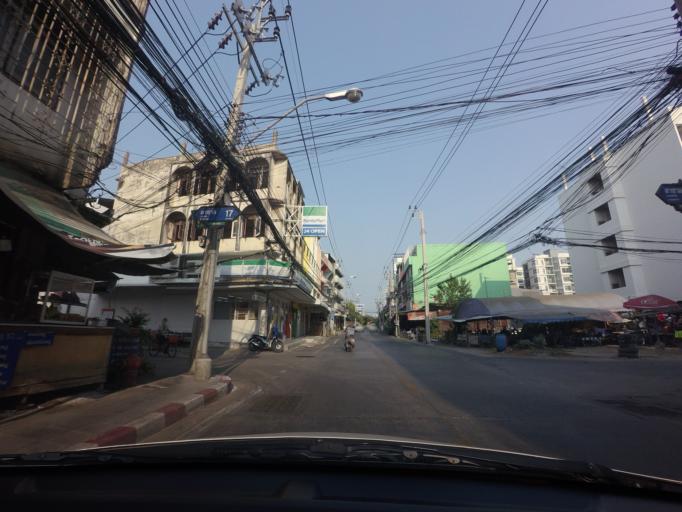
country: TH
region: Bangkok
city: Bang Na
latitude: 13.6606
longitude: 100.6104
